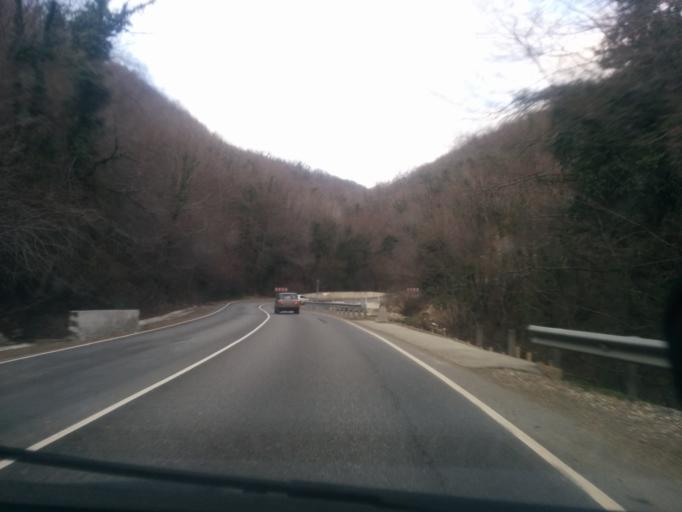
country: RU
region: Krasnodarskiy
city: Agoy
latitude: 44.1440
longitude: 39.0544
